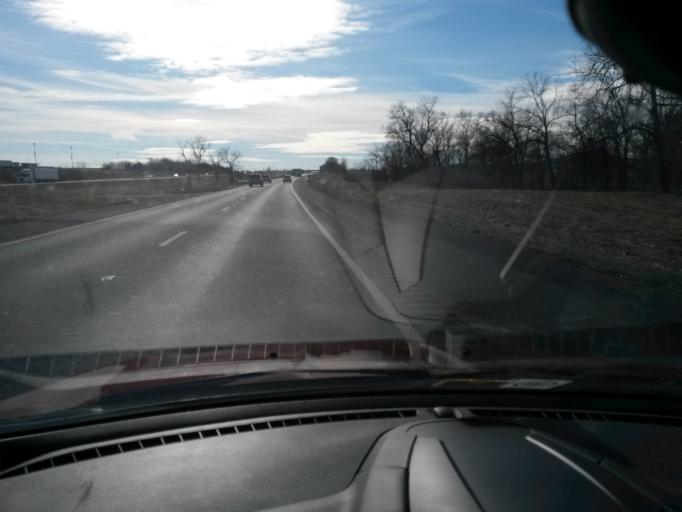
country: US
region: Virginia
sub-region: Rockingham County
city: Dayton
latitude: 38.3667
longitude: -78.9218
